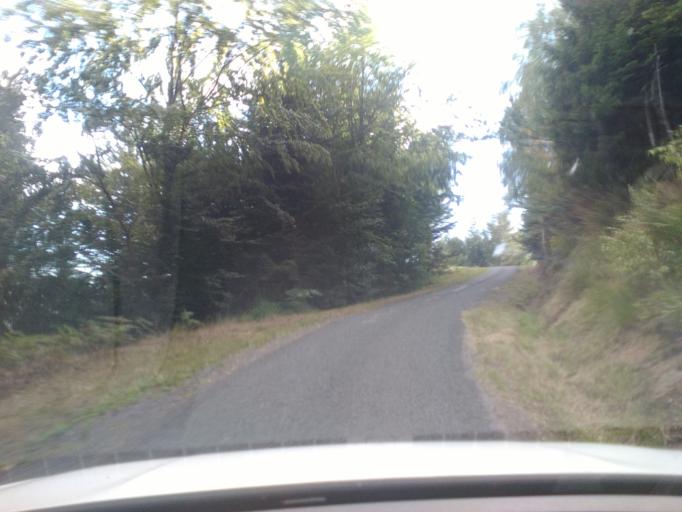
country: FR
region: Lorraine
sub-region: Departement des Vosges
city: Sainte-Marguerite
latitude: 48.3077
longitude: 7.0317
